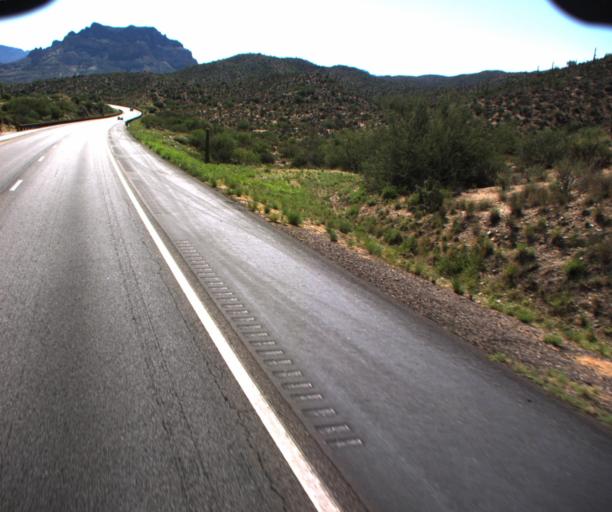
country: US
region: Arizona
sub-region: Pinal County
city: Gold Camp
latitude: 33.2736
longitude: -111.2217
